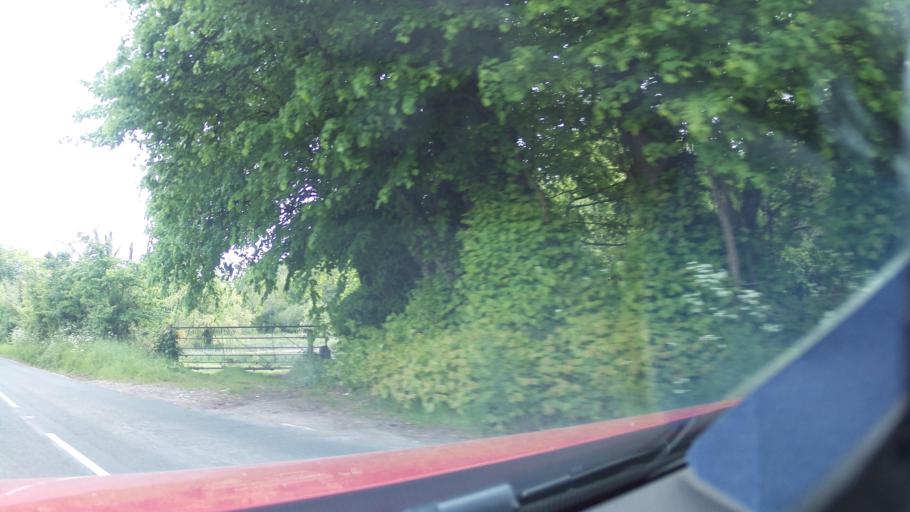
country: GB
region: England
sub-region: Dorset
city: Dorchester
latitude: 50.7614
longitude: -2.4762
